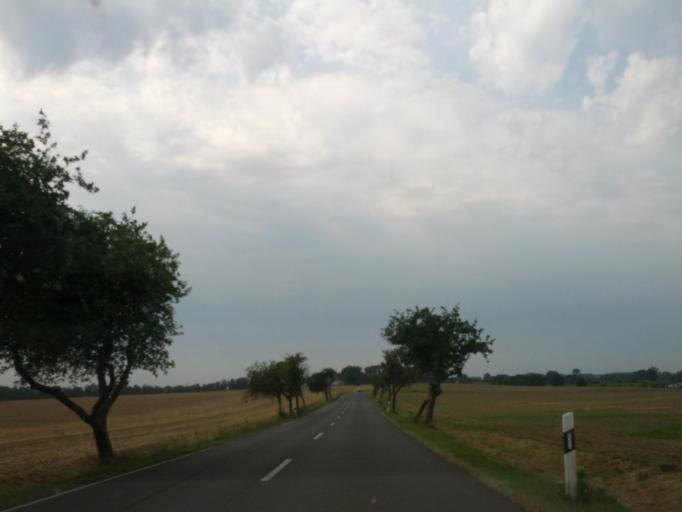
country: DE
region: Brandenburg
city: Kremmen
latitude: 52.7512
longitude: 12.9042
